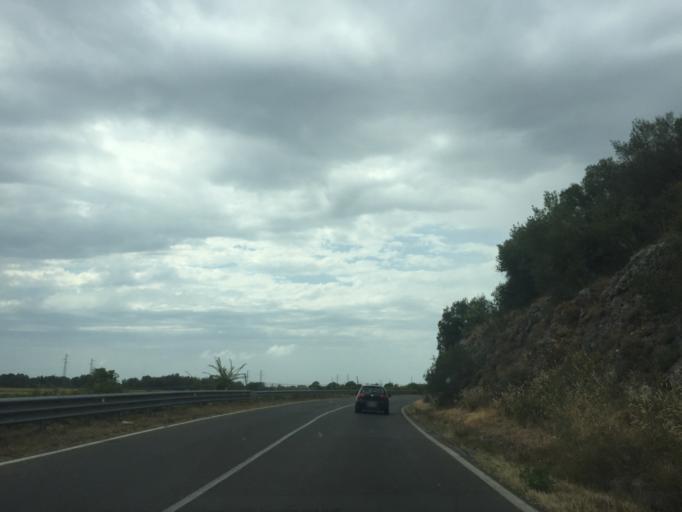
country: IT
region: Tuscany
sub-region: Province of Pisa
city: Asciano
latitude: 43.7412
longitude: 10.4702
